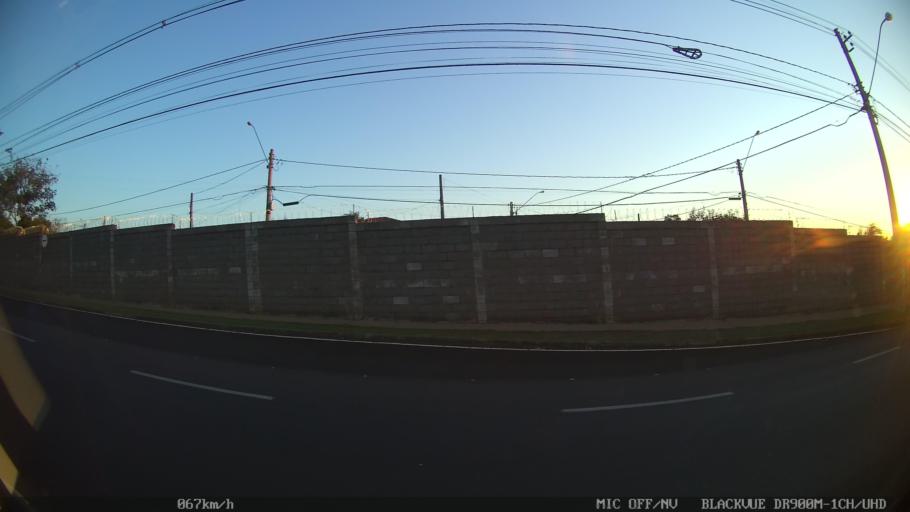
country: BR
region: Sao Paulo
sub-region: Sao Jose Do Rio Preto
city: Sao Jose do Rio Preto
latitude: -20.7768
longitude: -49.3464
